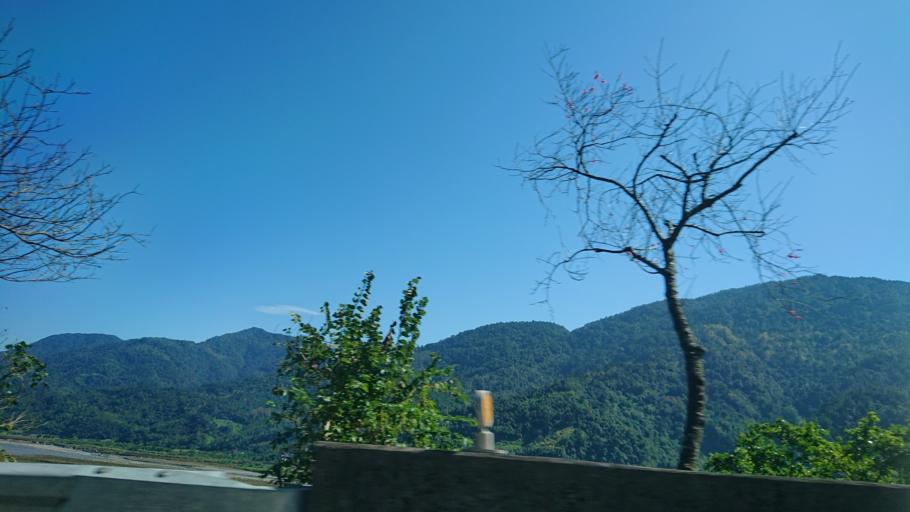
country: TW
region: Taiwan
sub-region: Yilan
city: Yilan
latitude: 24.5907
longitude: 121.5069
